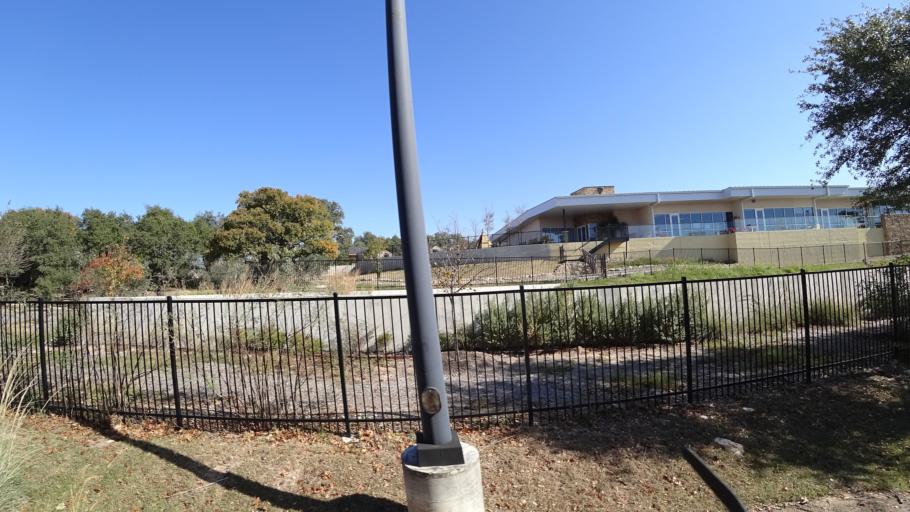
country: US
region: Texas
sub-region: Williamson County
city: Anderson Mill
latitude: 30.3947
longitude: -97.8495
